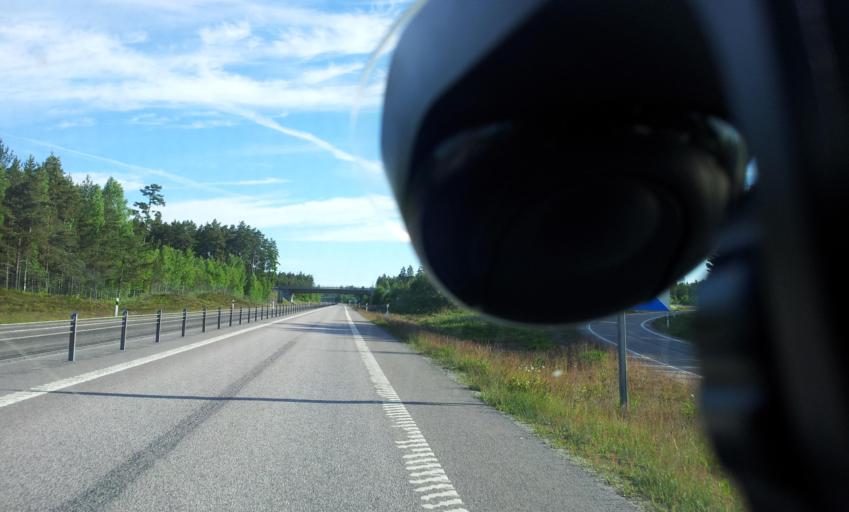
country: SE
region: Kalmar
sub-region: Torsas Kommun
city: Torsas
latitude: 56.4994
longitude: 16.0861
